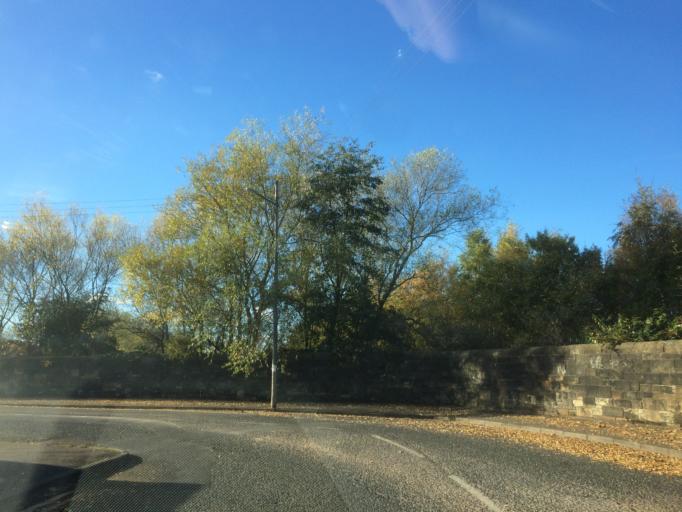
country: GB
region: Scotland
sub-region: Glasgow City
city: Glasgow
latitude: 55.8573
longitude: -4.2337
